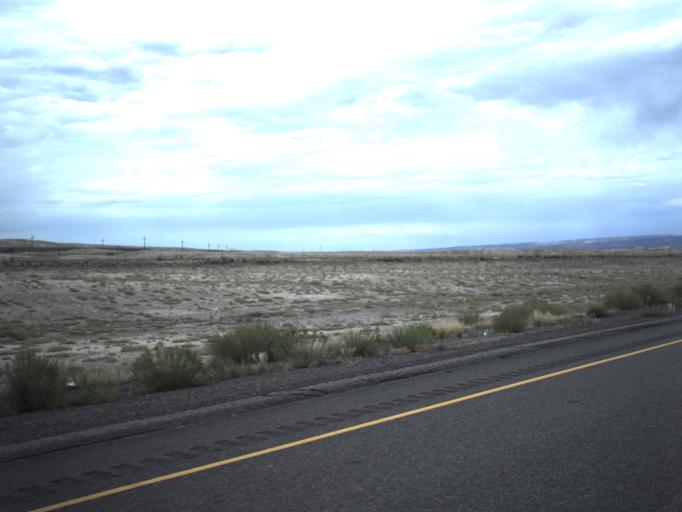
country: US
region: Utah
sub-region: Grand County
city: Moab
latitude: 38.9326
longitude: -109.4419
